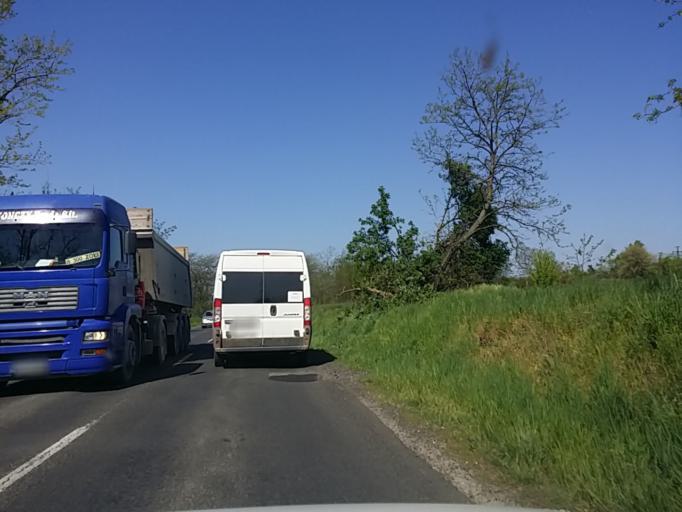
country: HU
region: Pest
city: Mogyorod
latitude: 47.6012
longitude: 19.2157
